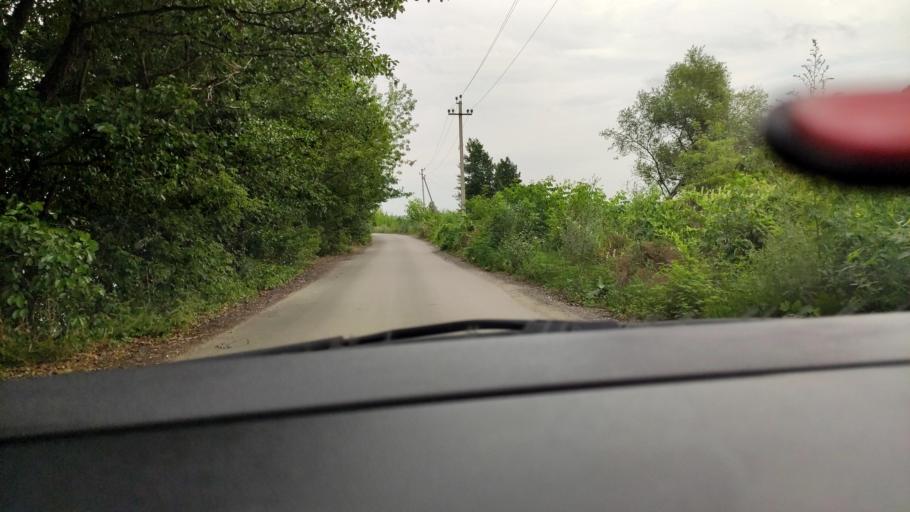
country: RU
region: Voronezj
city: Ramon'
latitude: 51.8947
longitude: 39.3516
